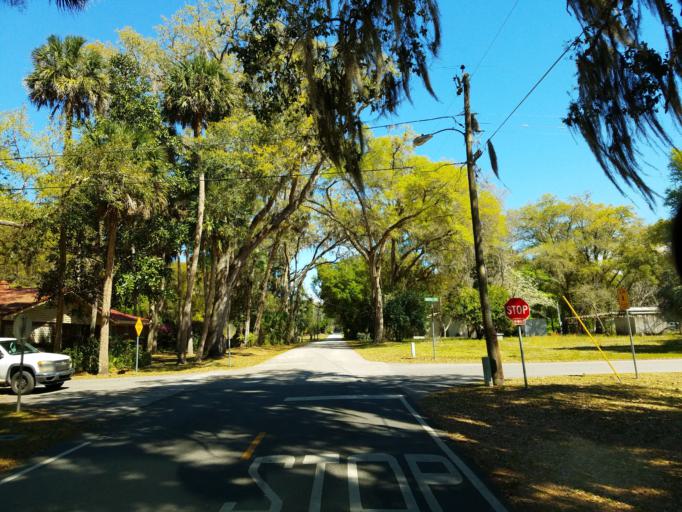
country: US
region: Florida
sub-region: Sumter County
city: Lake Panasoffkee
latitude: 28.8017
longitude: -82.0583
